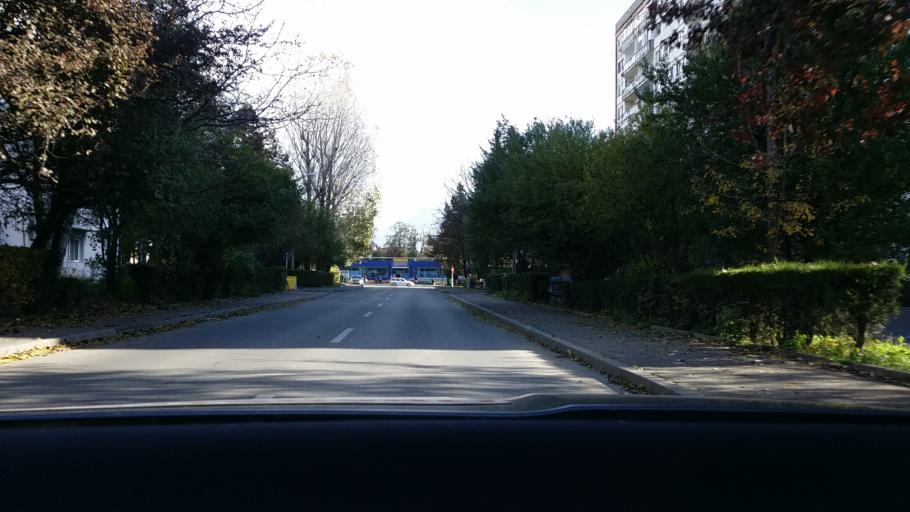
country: RO
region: Prahova
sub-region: Municipiul Campina
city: Campina
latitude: 45.1191
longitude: 25.7377
